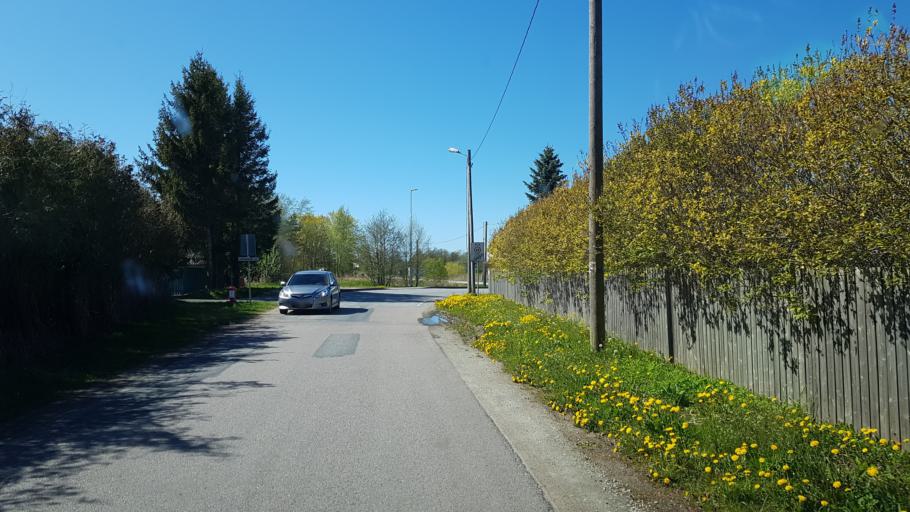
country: EE
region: Harju
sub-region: Viimsi vald
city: Viimsi
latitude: 59.5471
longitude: 24.8799
